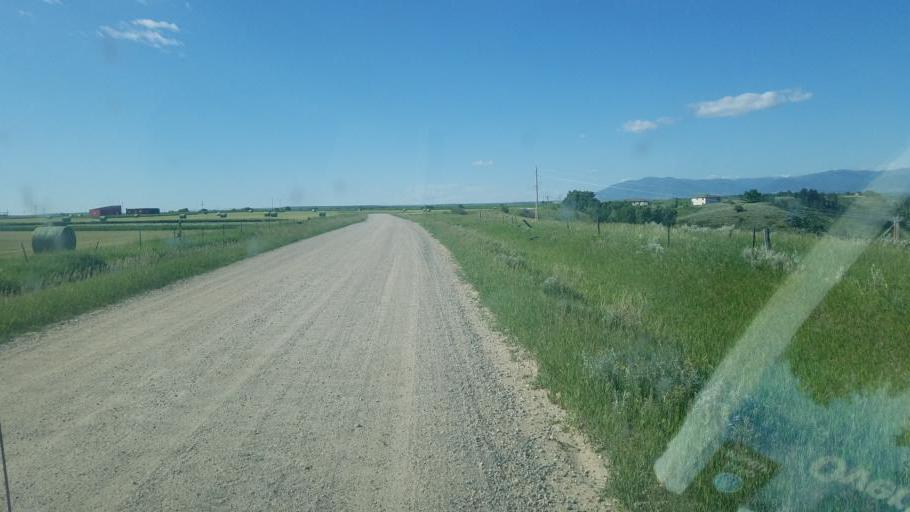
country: US
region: Montana
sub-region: Carbon County
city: Red Lodge
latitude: 45.3536
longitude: -109.1597
